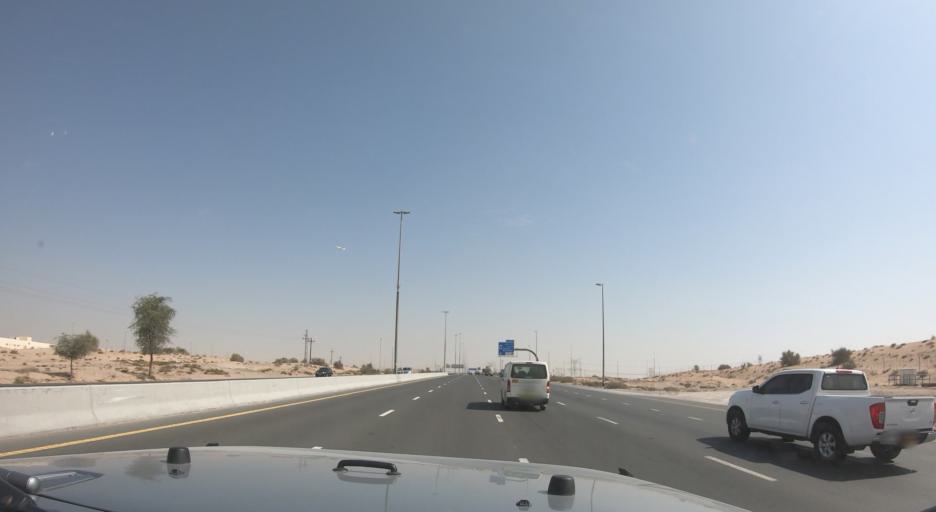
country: AE
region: Ash Shariqah
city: Sharjah
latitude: 25.1648
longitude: 55.4883
